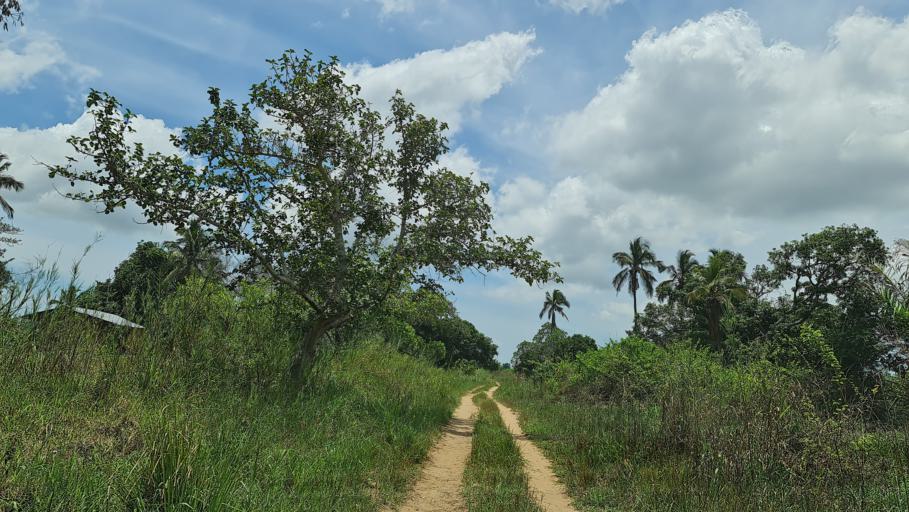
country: MZ
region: Zambezia
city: Quelimane
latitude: -17.5791
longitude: 37.3746
